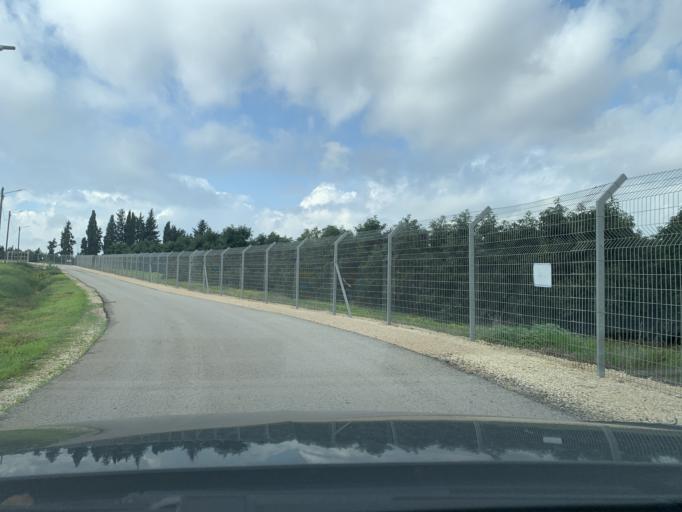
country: PS
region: West Bank
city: Qalqilyah
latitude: 32.2002
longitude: 34.9504
